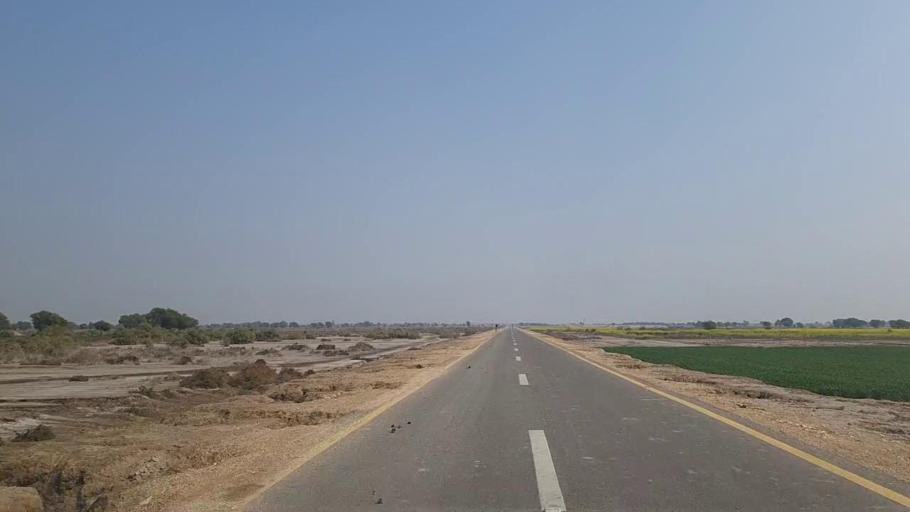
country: PK
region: Sindh
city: Jam Sahib
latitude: 26.3724
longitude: 68.5217
